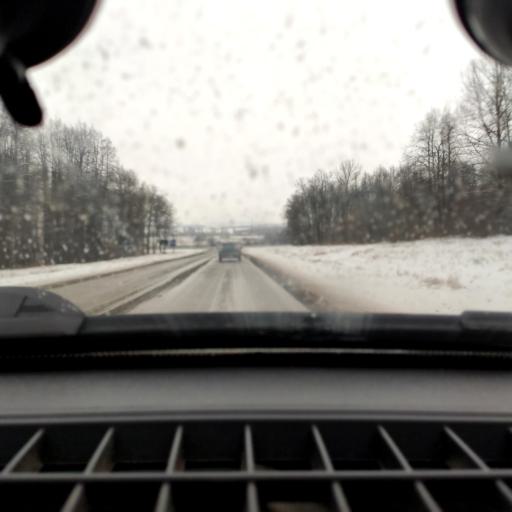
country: RU
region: Bashkortostan
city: Iglino
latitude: 54.7662
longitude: 56.4131
